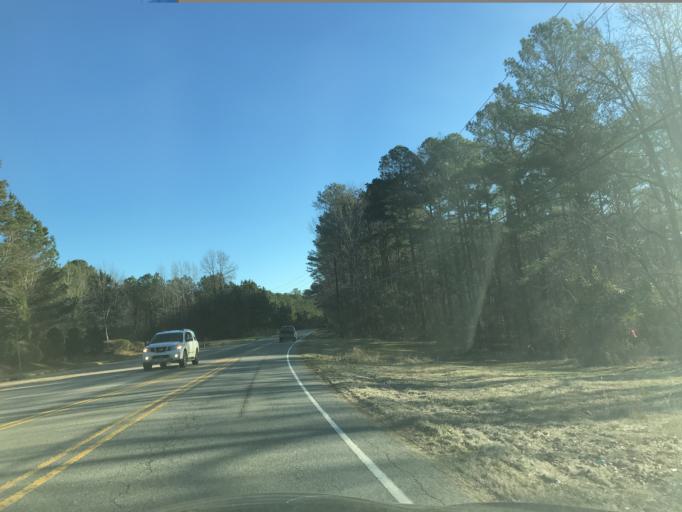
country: US
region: North Carolina
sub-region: Wake County
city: Cary
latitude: 35.9074
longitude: -78.7185
